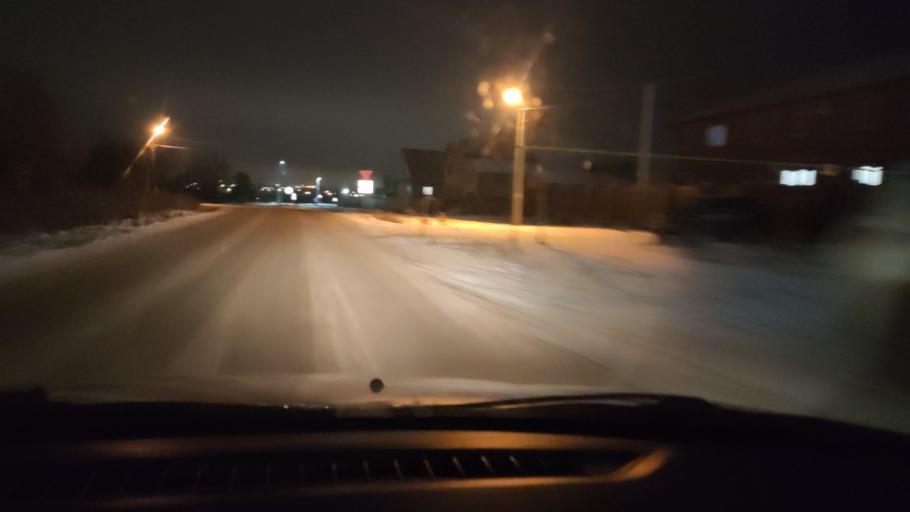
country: RU
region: Perm
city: Ferma
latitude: 57.8947
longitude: 56.3269
